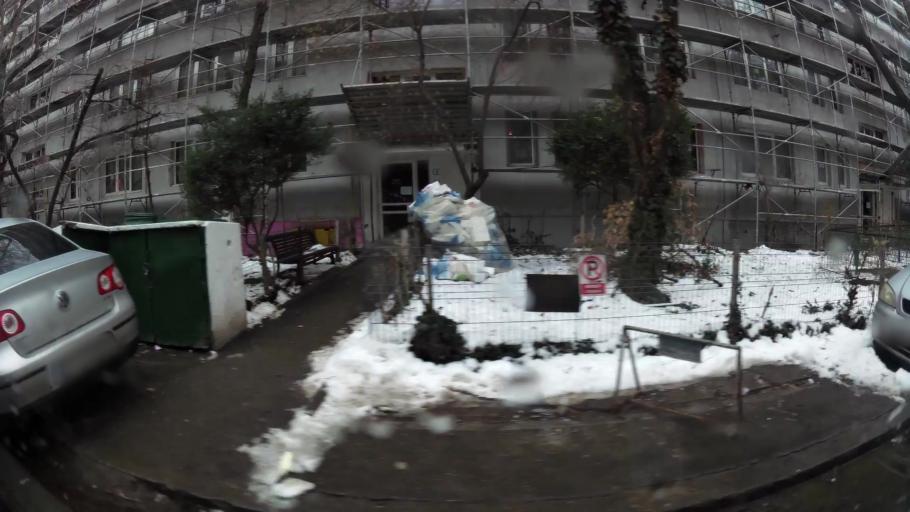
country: RO
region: Ilfov
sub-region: Comuna Chiajna
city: Rosu
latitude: 44.4243
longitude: 26.0222
